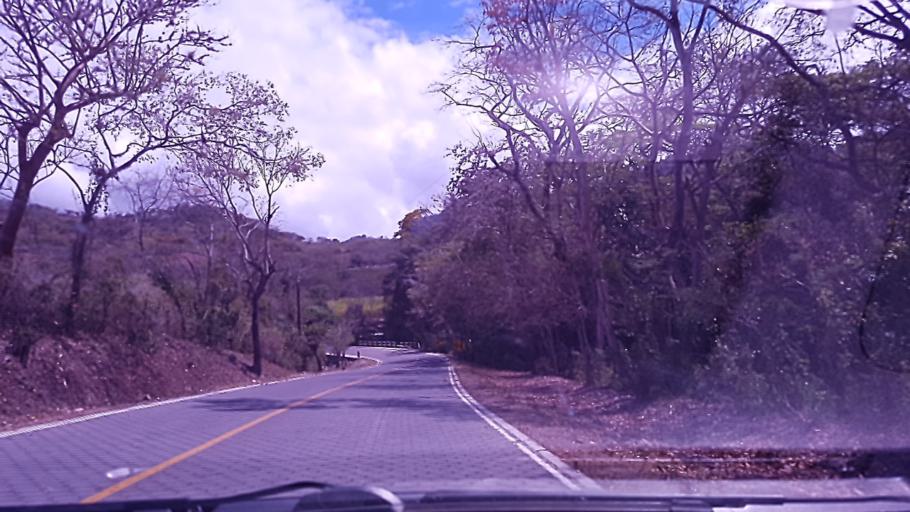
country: NI
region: Esteli
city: Condega
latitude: 13.4051
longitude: -86.2941
